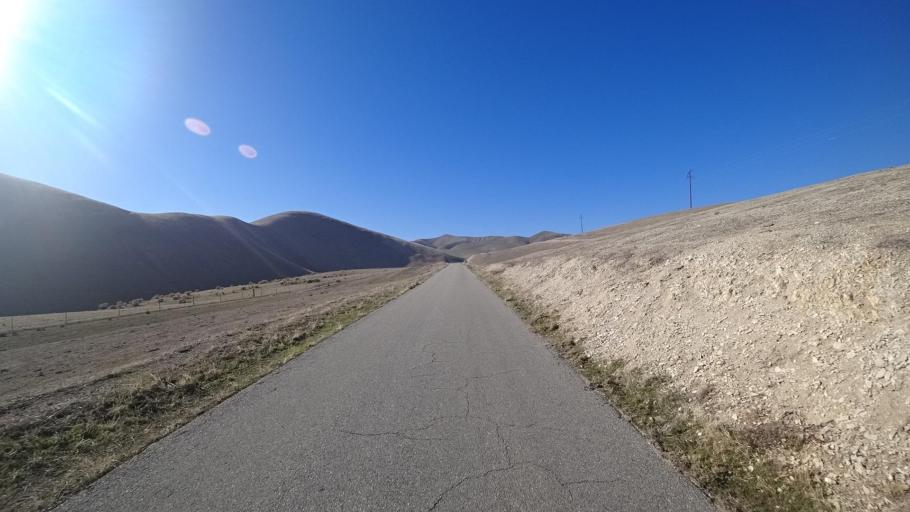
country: US
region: California
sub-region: Kern County
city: Taft Heights
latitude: 35.2310
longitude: -119.6645
